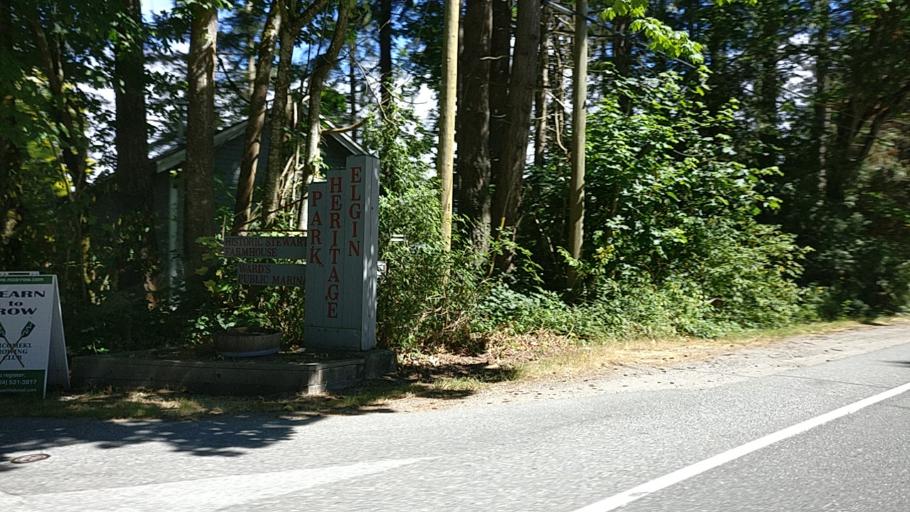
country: CA
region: British Columbia
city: Surrey
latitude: 49.0644
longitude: -122.8424
